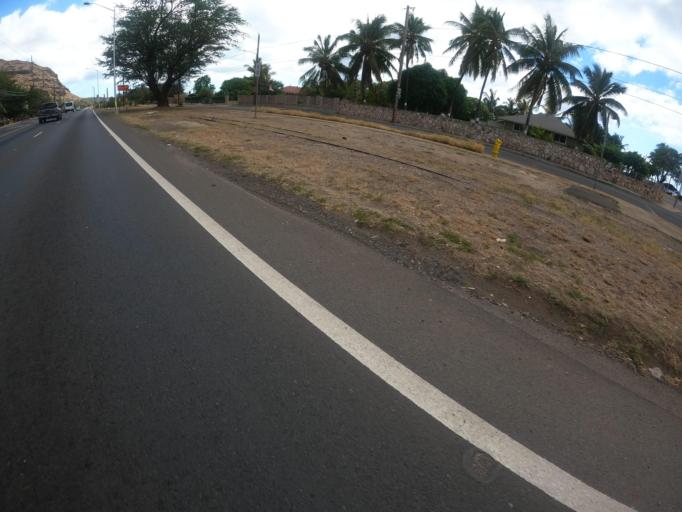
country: US
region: Hawaii
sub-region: Honolulu County
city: Nanakuli
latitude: 21.3750
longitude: -158.1393
